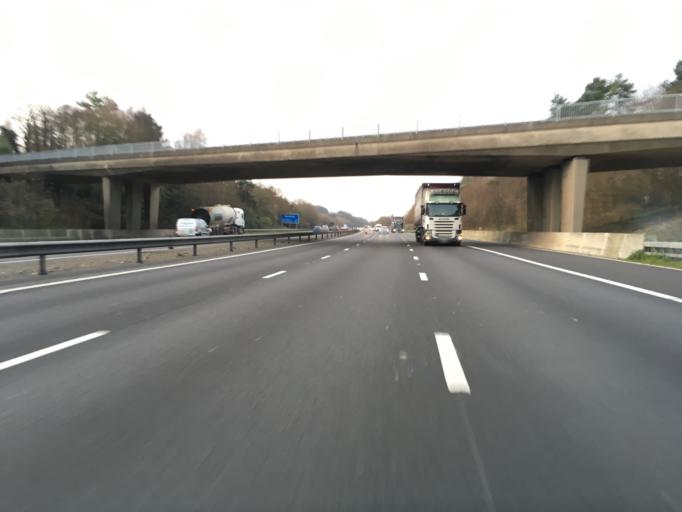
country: GB
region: England
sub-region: Gloucestershire
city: Barnwood
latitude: 51.8357
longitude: -2.2019
